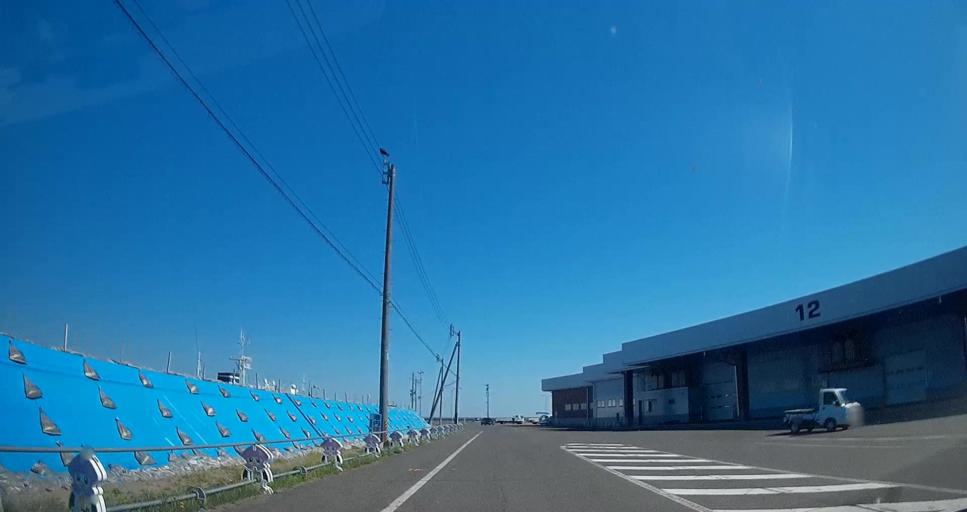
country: JP
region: Aomori
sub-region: Hachinohe Shi
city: Uchimaru
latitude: 40.5287
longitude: 141.5360
